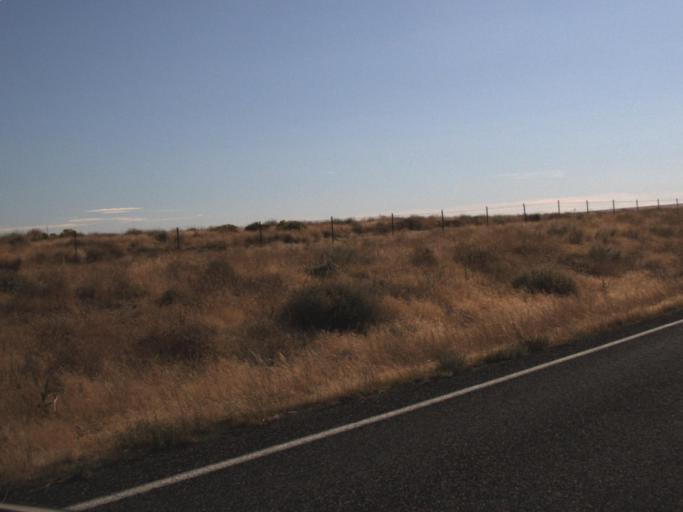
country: US
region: Washington
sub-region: Grant County
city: Desert Aire
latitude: 46.5346
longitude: -119.6836
